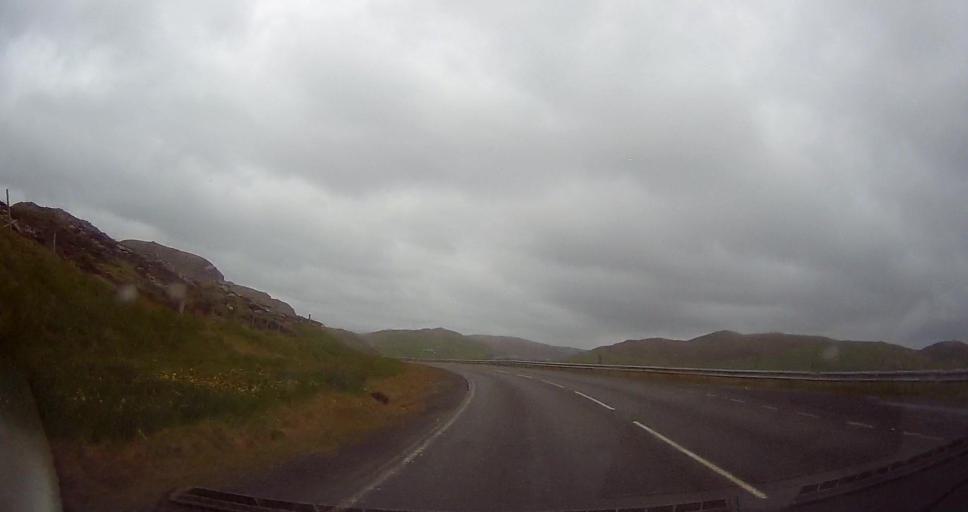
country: GB
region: Scotland
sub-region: Shetland Islands
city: Lerwick
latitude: 60.4151
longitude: -1.3926
